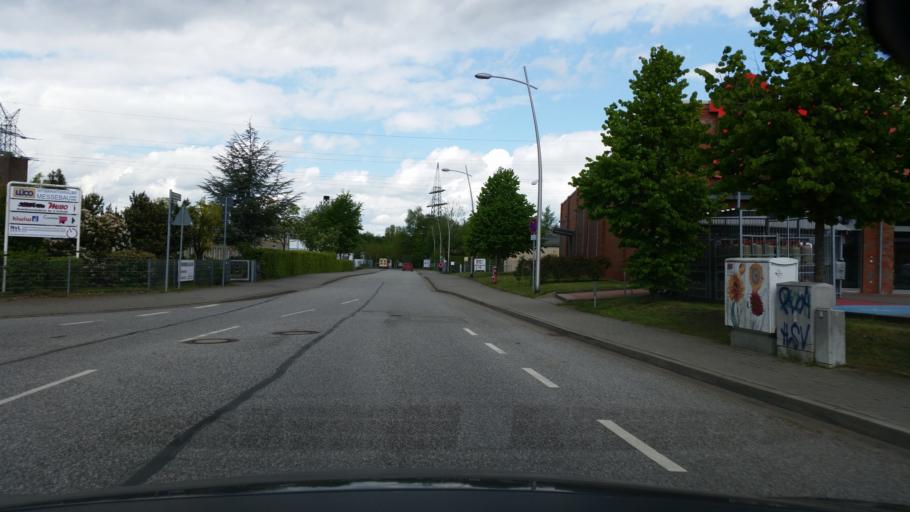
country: DE
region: Schleswig-Holstein
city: Norderstedt
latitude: 53.7099
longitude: 10.0195
